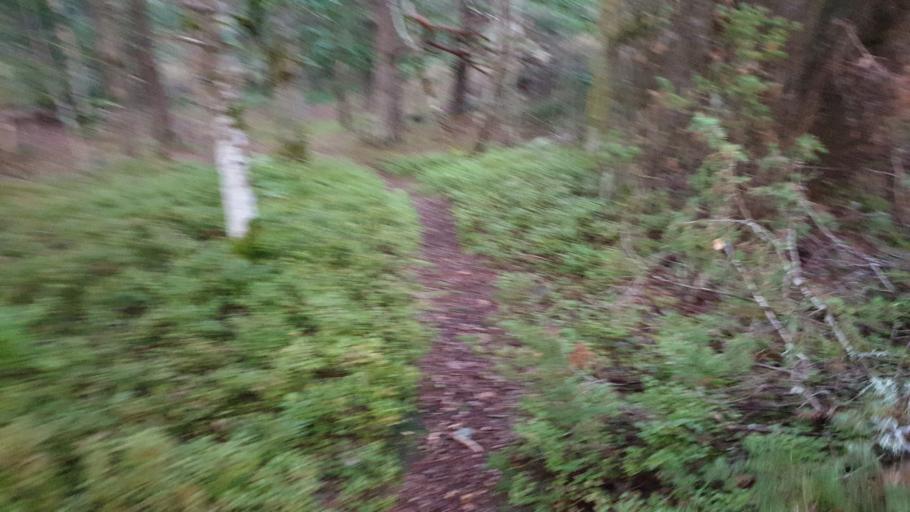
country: SE
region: Vaestra Goetaland
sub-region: Goteborg
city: Billdal
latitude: 57.5917
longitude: 11.9111
